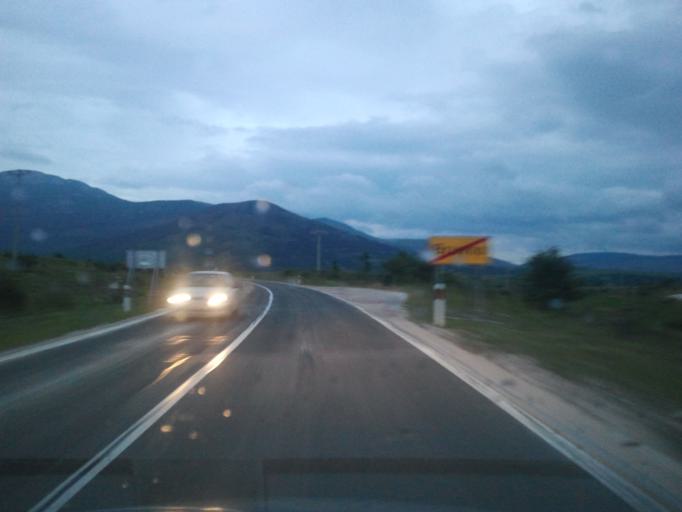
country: HR
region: Zadarska
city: Gracac
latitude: 44.4069
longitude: 15.8961
